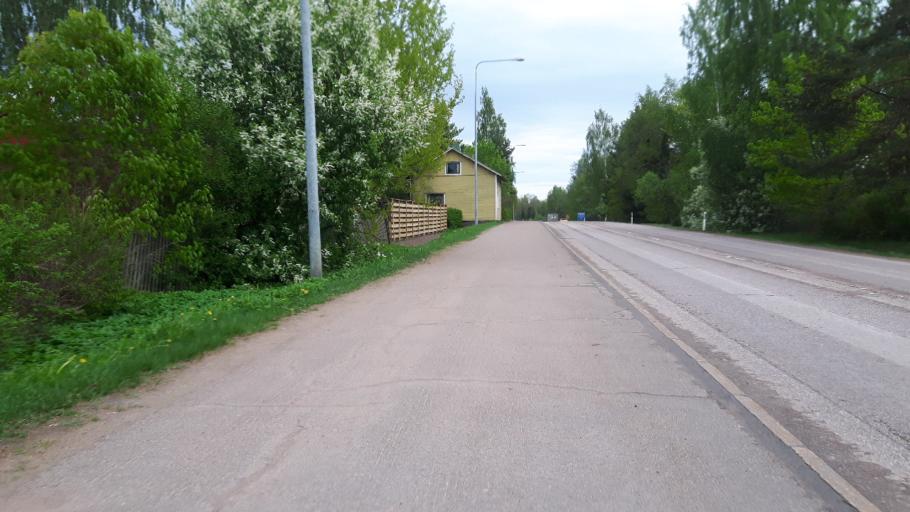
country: FI
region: Kymenlaakso
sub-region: Kotka-Hamina
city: Hamina
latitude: 60.5601
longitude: 27.2275
